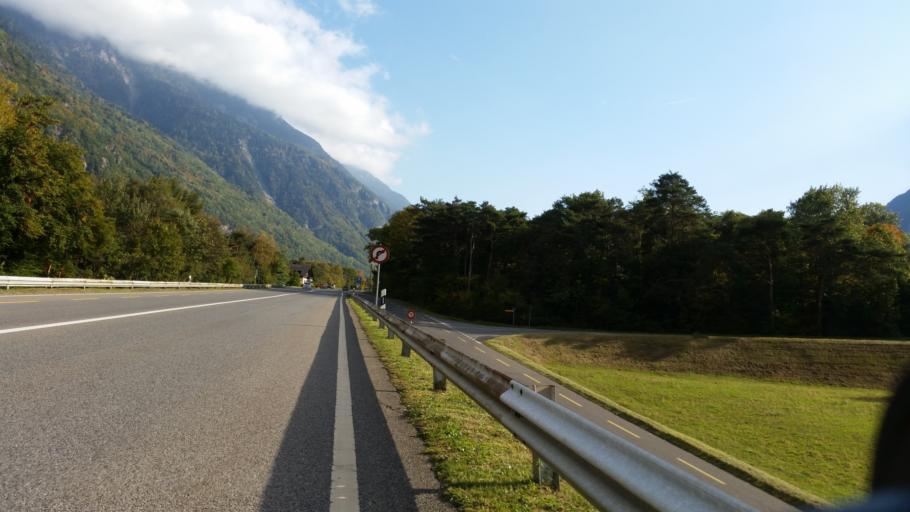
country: CH
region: Valais
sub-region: Martigny District
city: Evionnaz
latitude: 46.1989
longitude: 7.0187
